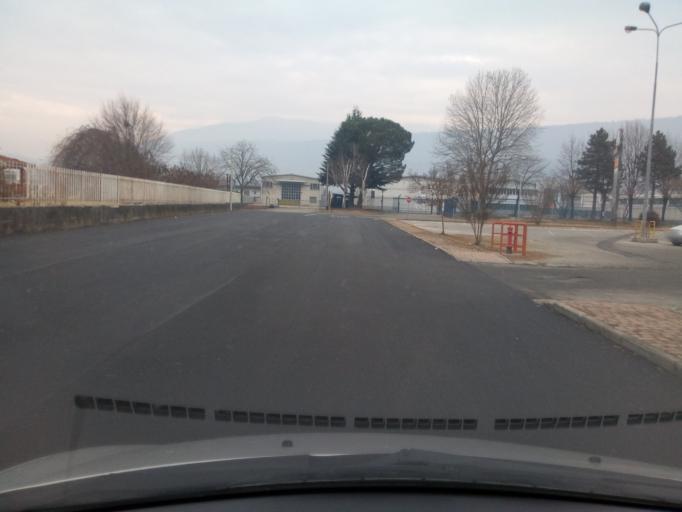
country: IT
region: Piedmont
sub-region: Provincia di Torino
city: Burolo
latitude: 45.4714
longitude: 7.9270
